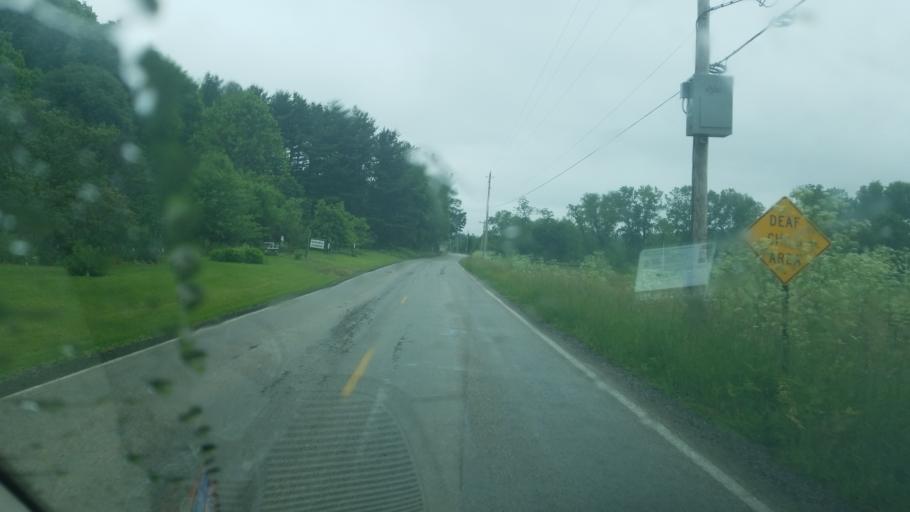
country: US
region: Ohio
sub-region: Sandusky County
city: Bellville
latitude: 40.6715
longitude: -82.4338
